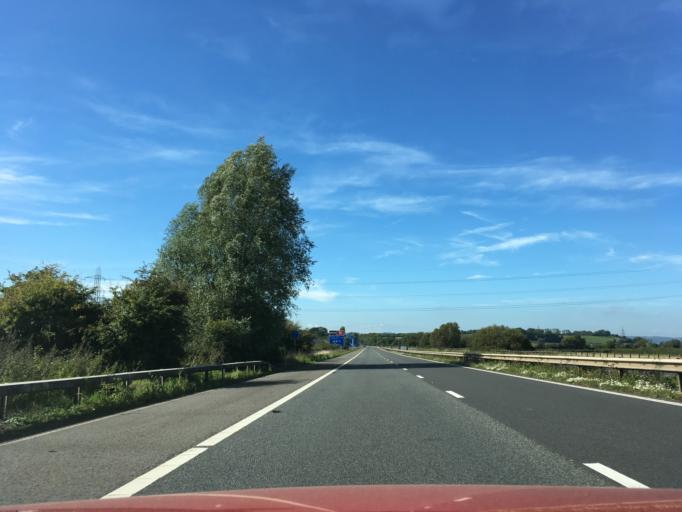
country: GB
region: England
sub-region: South Gloucestershire
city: Almondsbury
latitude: 51.5911
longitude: -2.6025
